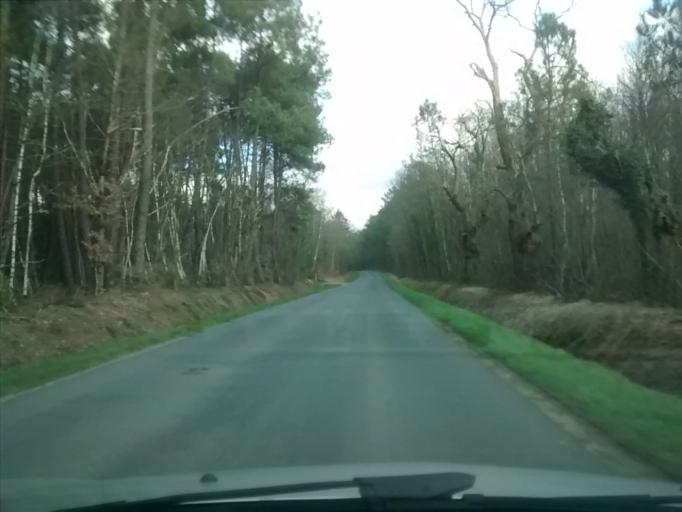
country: FR
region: Pays de la Loire
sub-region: Departement de la Sarthe
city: Bouloire
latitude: 47.9448
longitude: 0.5000
